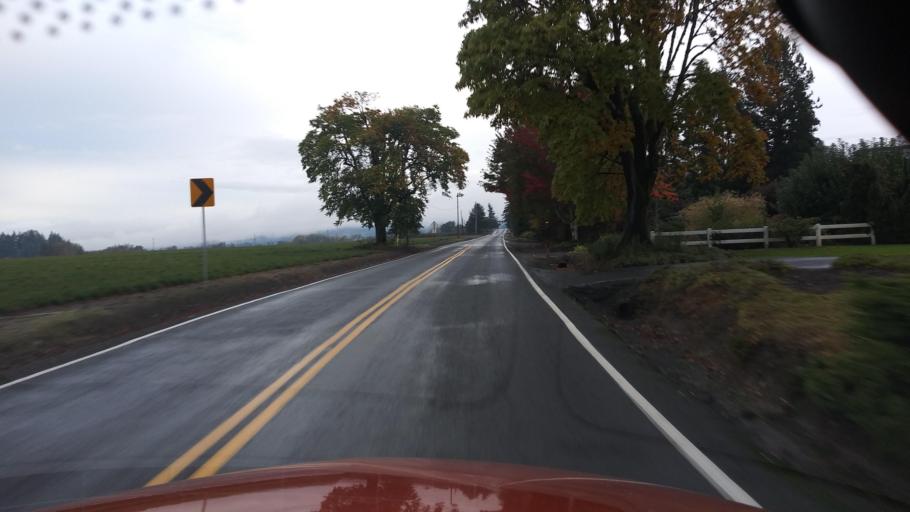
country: US
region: Oregon
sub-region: Washington County
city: North Plains
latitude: 45.5924
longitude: -123.0154
